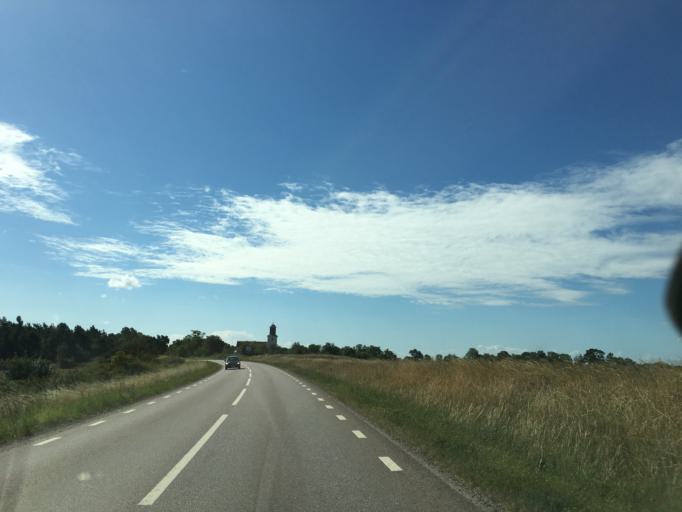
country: SE
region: Kalmar
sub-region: Morbylanga Kommun
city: Moerbylanga
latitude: 56.5455
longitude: 16.4429
